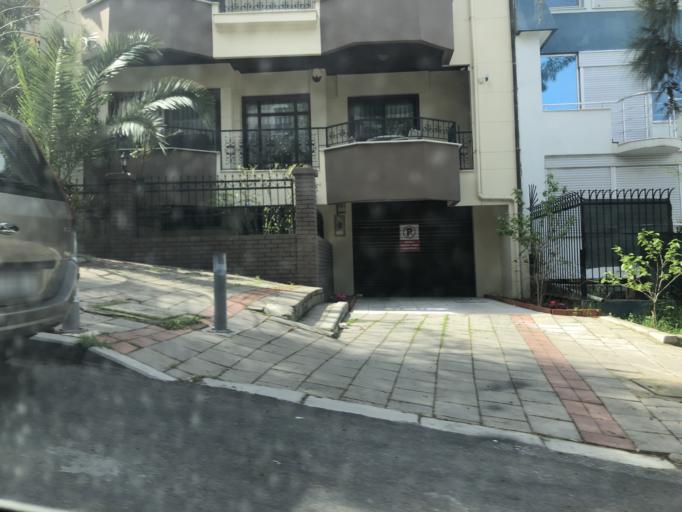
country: TR
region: Izmir
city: Karabaglar
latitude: 38.3920
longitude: 27.0447
